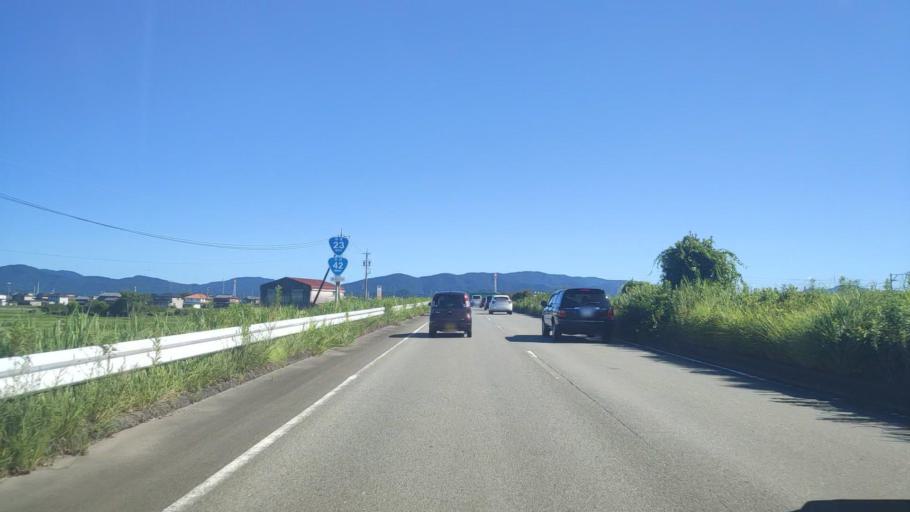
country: JP
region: Mie
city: Ise
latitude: 34.5237
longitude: 136.6845
